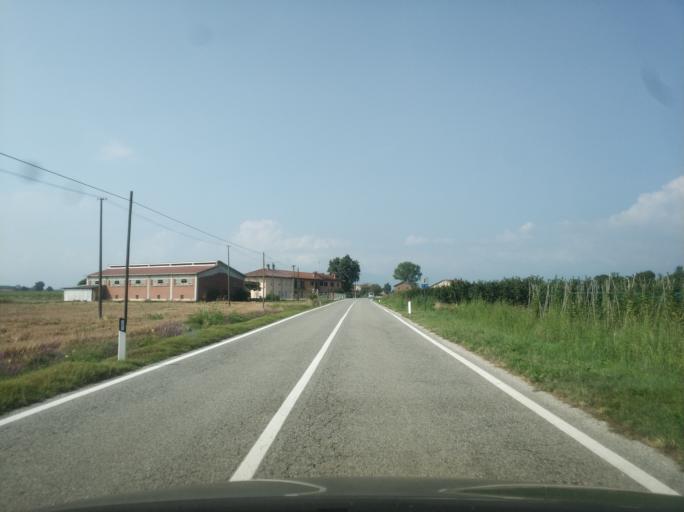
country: IT
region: Piedmont
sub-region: Provincia di Cuneo
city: Tarantasca
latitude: 44.4922
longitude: 7.5557
